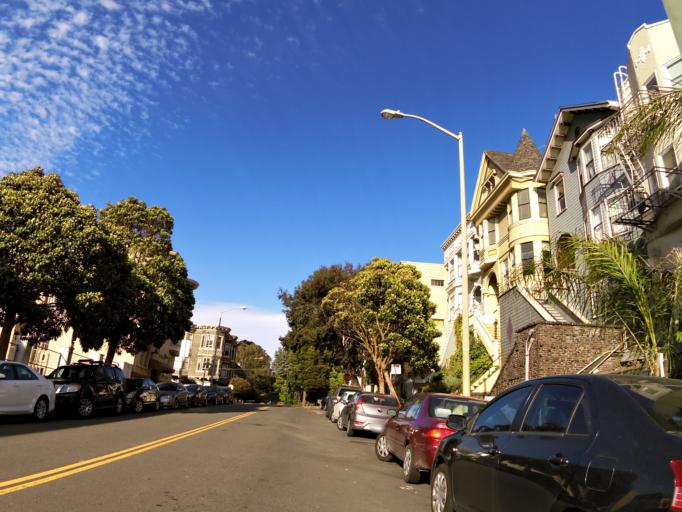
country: US
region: California
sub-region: San Francisco County
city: San Francisco
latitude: 37.7694
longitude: -122.4442
